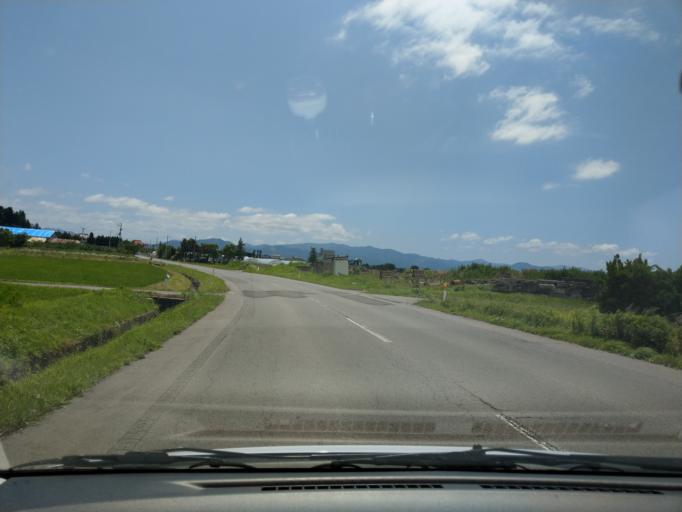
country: JP
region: Aomori
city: Kuroishi
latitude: 40.6218
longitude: 140.5621
